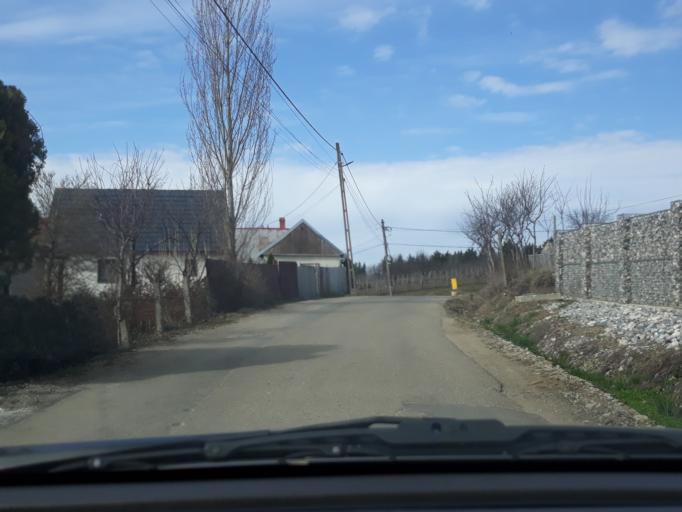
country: RO
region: Bihor
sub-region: Comuna Paleu
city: Paleu
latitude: 47.1115
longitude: 21.9584
